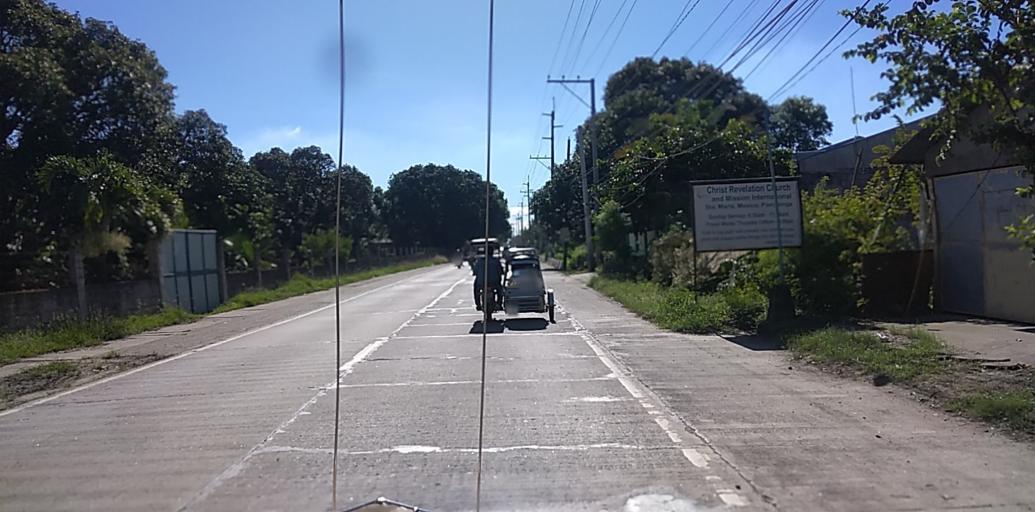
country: PH
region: Central Luzon
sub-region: Province of Pampanga
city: Santo Domingo
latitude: 15.0653
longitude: 120.7684
